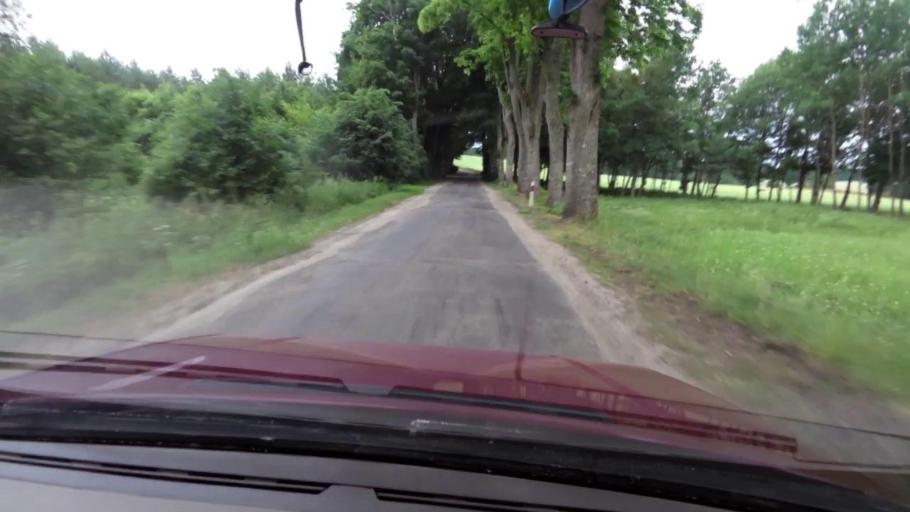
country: PL
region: Pomeranian Voivodeship
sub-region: Powiat slupski
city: Kepice
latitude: 54.1918
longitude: 16.7976
